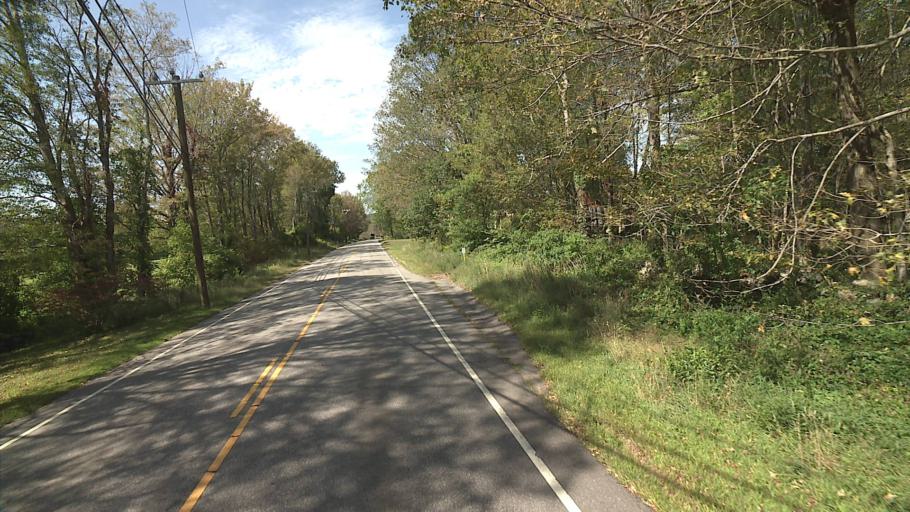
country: US
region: Connecticut
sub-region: Windham County
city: Willimantic
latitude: 41.6886
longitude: -72.2868
